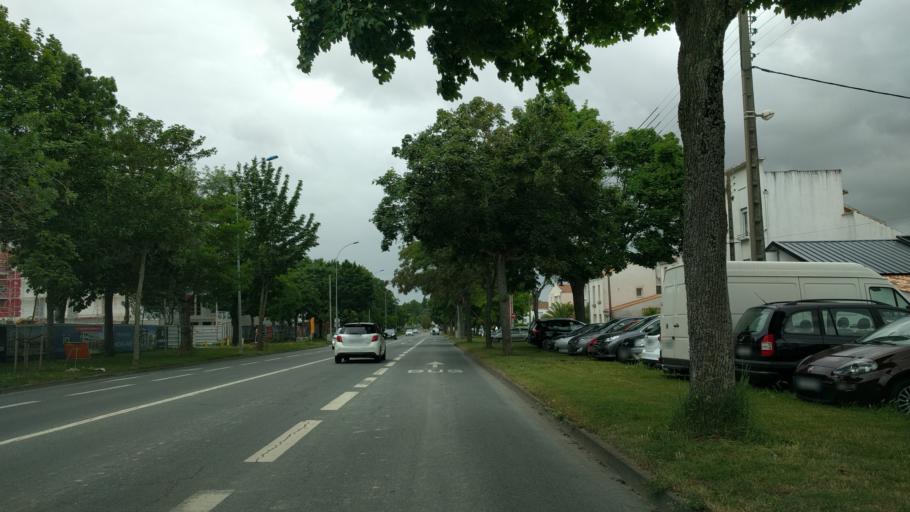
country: FR
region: Poitou-Charentes
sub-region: Departement de la Charente-Maritime
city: La Rochelle
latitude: 46.1683
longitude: -1.1431
